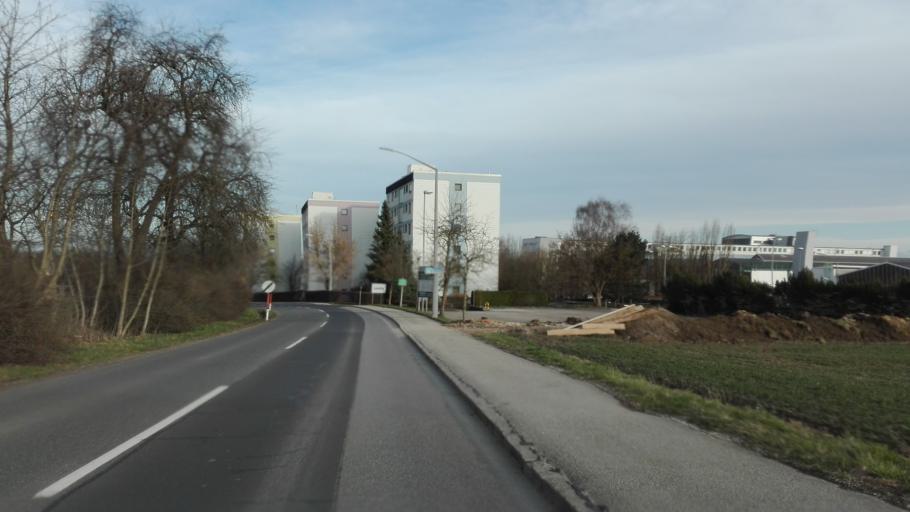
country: AT
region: Upper Austria
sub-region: Politischer Bezirk Linz-Land
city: Leonding
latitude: 48.2767
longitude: 14.2287
